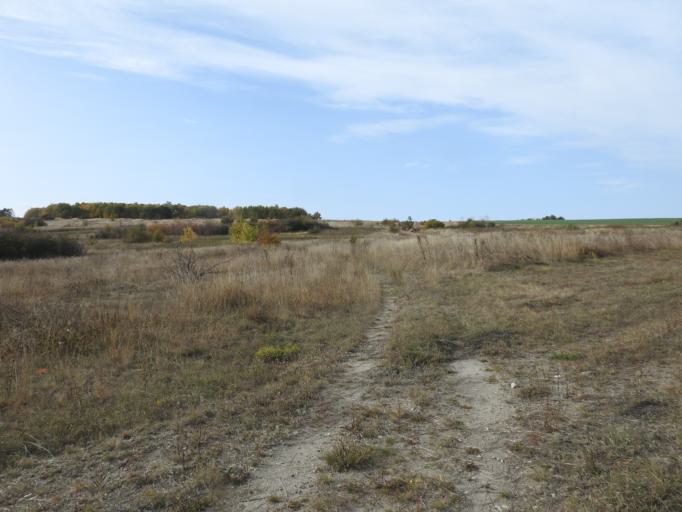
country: RU
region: Saratov
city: Baltay
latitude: 52.5172
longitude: 46.6815
